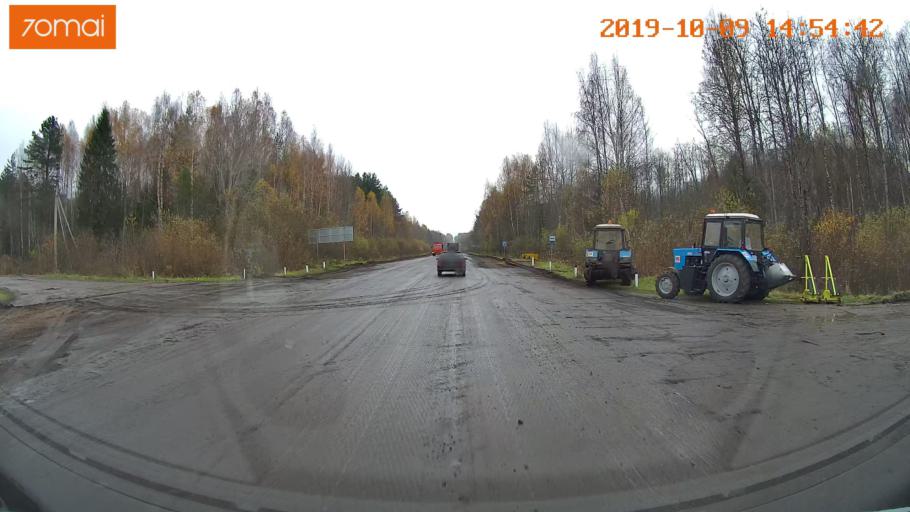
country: RU
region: Kostroma
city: Chistyye Bory
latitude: 58.3547
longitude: 41.6436
